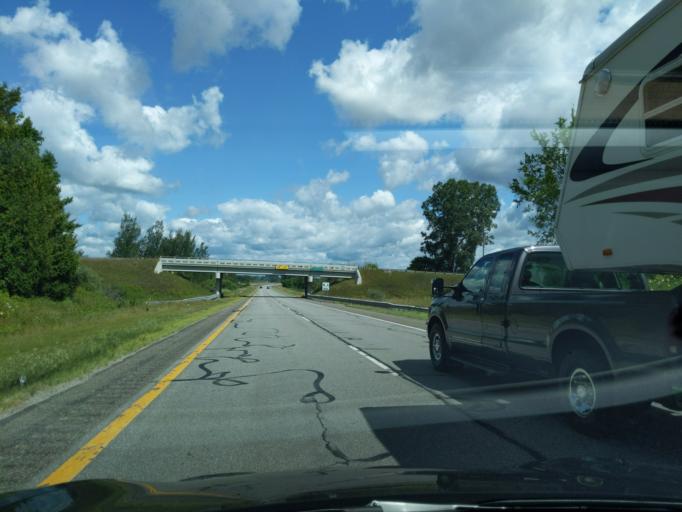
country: US
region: Michigan
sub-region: Clare County
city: Clare
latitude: 43.7558
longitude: -84.7573
